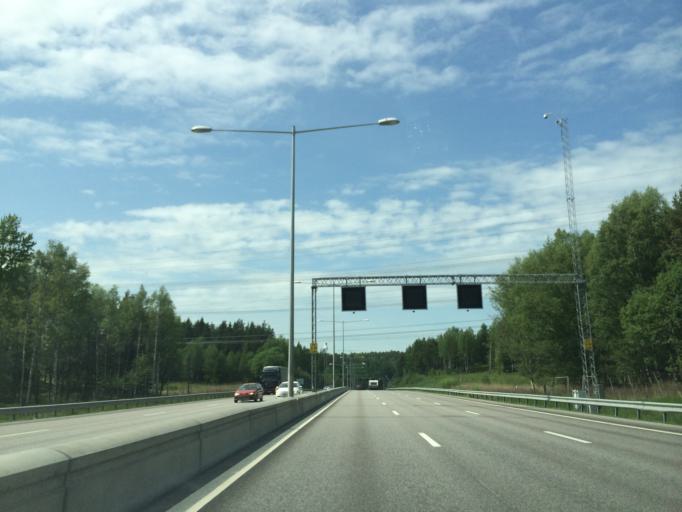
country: SE
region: Stockholm
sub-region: Salems Kommun
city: Ronninge
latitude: 59.2083
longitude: 17.7095
